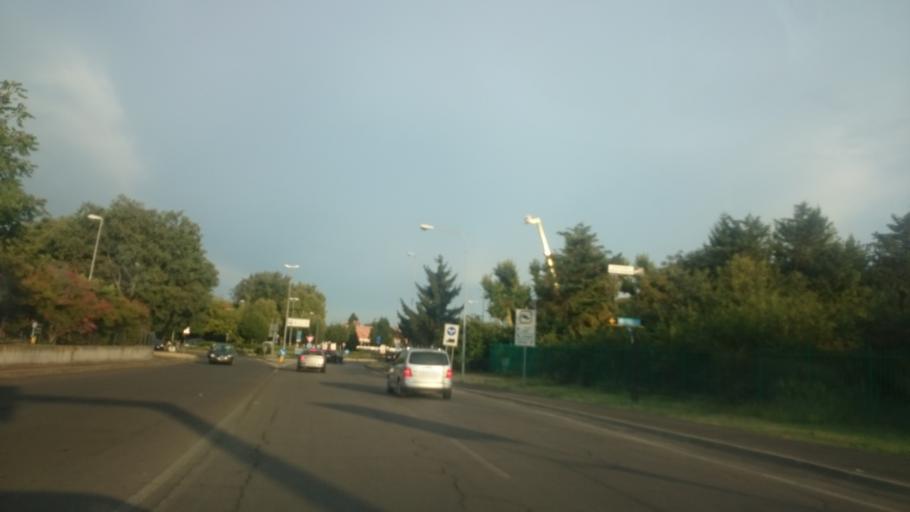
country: IT
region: Emilia-Romagna
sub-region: Provincia di Reggio Emilia
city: Reggio nell'Emilia
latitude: 44.7080
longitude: 10.6379
